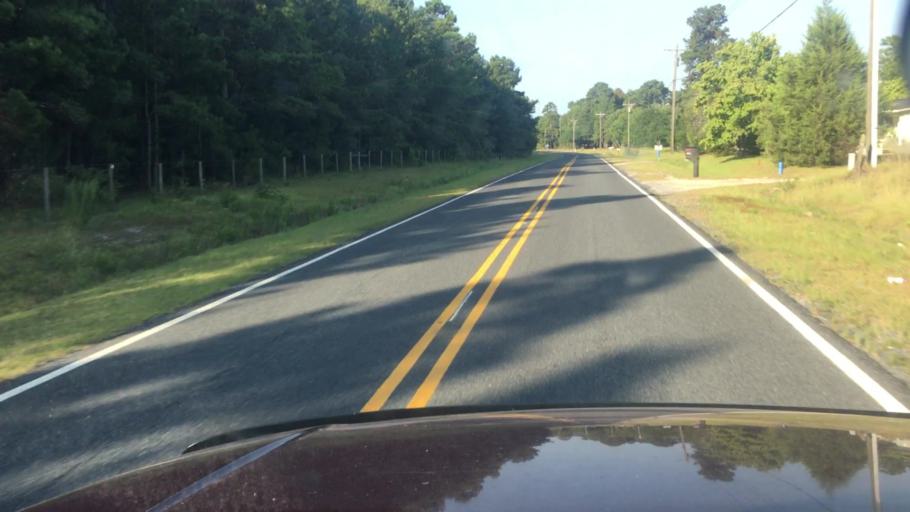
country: US
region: North Carolina
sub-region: Robeson County
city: Saint Pauls
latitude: 34.8536
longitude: -78.8535
